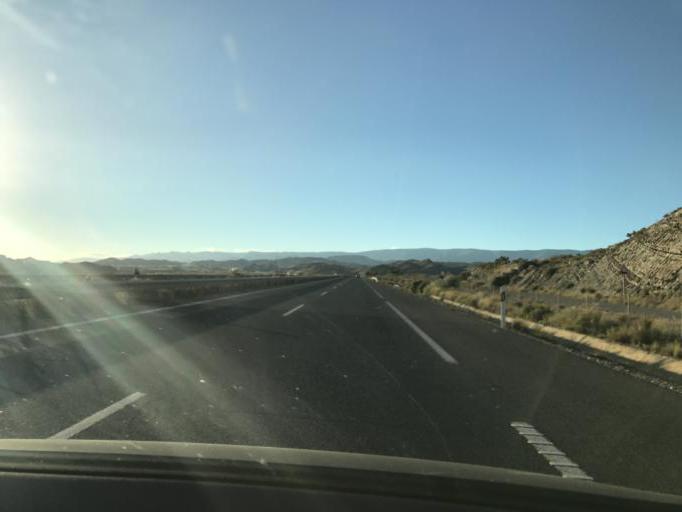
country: ES
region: Andalusia
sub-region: Provincia de Almeria
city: Tabernas
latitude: 37.0453
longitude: -2.4711
